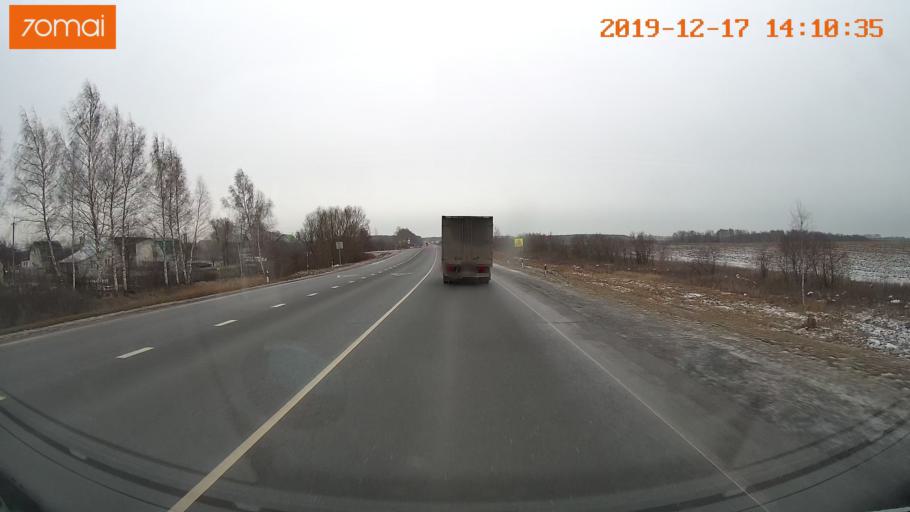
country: RU
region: Rjazan
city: Rybnoye
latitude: 54.5467
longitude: 39.5173
